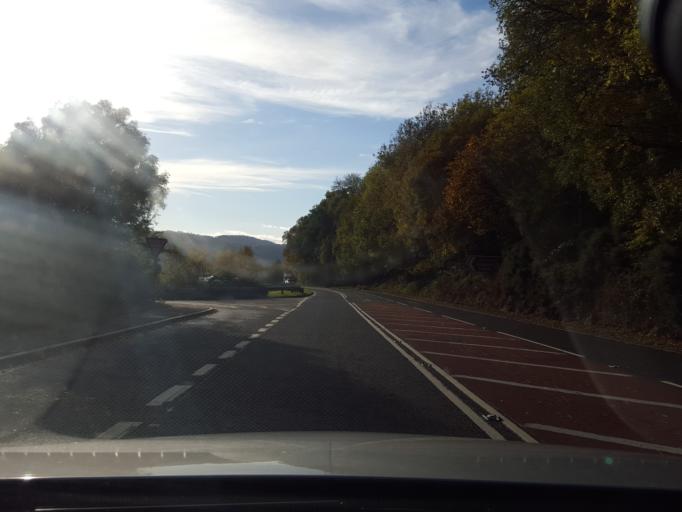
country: GB
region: Scotland
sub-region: Highland
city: Beauly
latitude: 57.3255
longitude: -4.4454
